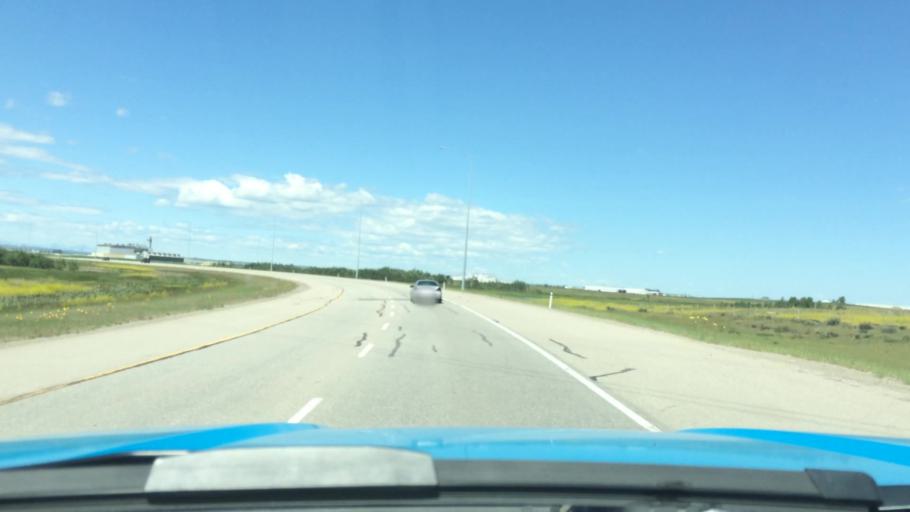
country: CA
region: Alberta
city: Airdrie
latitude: 51.1767
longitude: -113.9167
